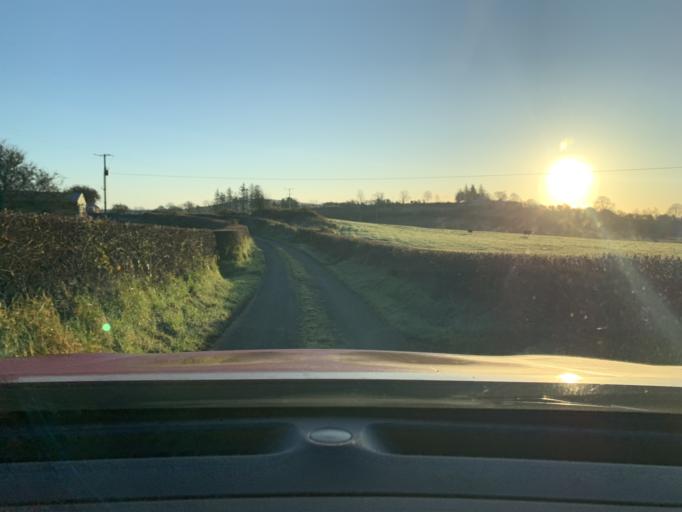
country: IE
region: Connaught
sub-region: Sligo
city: Ballymote
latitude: 54.0673
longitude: -8.5415
